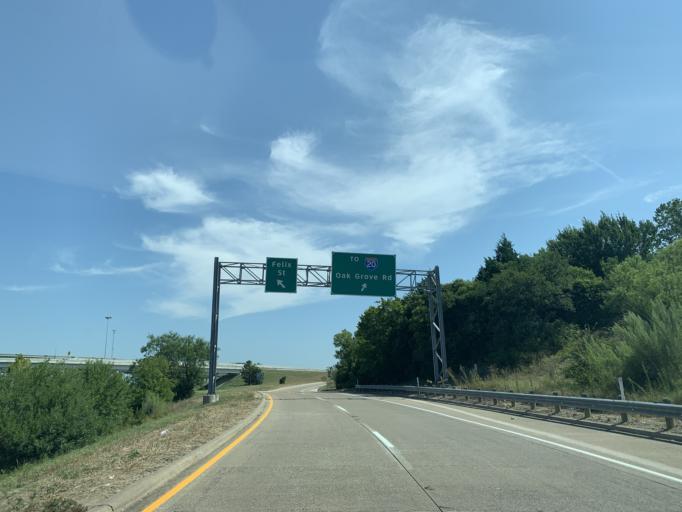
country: US
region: Texas
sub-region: Tarrant County
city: Edgecliff Village
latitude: 32.6650
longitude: -97.3175
